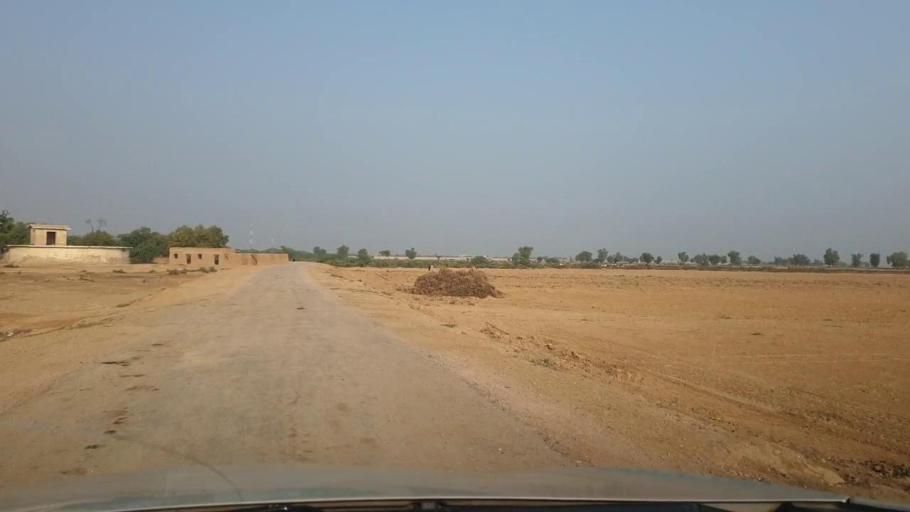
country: PK
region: Sindh
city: Sehwan
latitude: 26.3349
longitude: 67.7315
